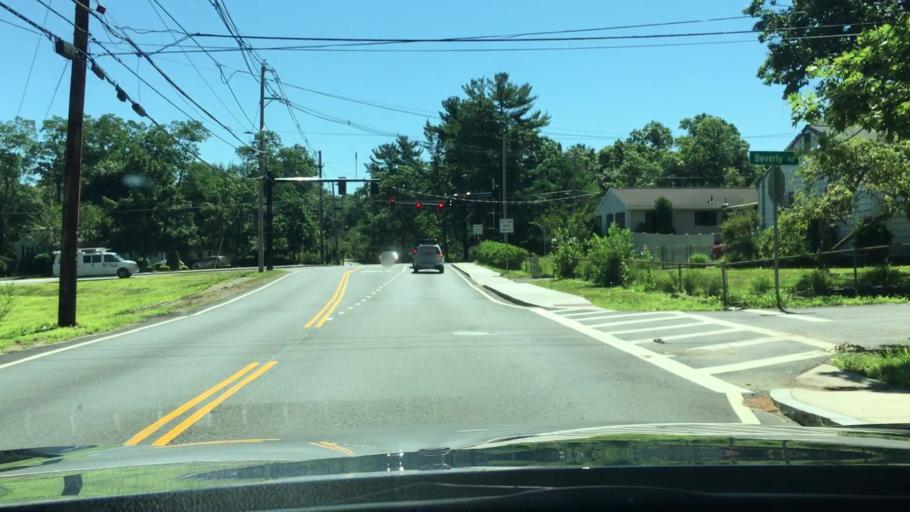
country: US
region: Massachusetts
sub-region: Middlesex County
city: Billerica
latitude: 42.5745
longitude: -71.2631
